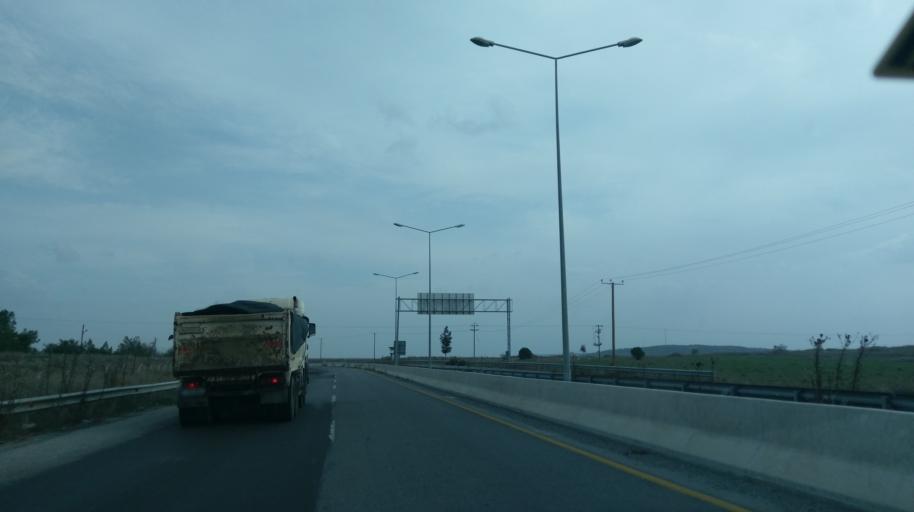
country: CY
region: Lefkosia
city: Mammari
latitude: 35.2158
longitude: 33.1824
